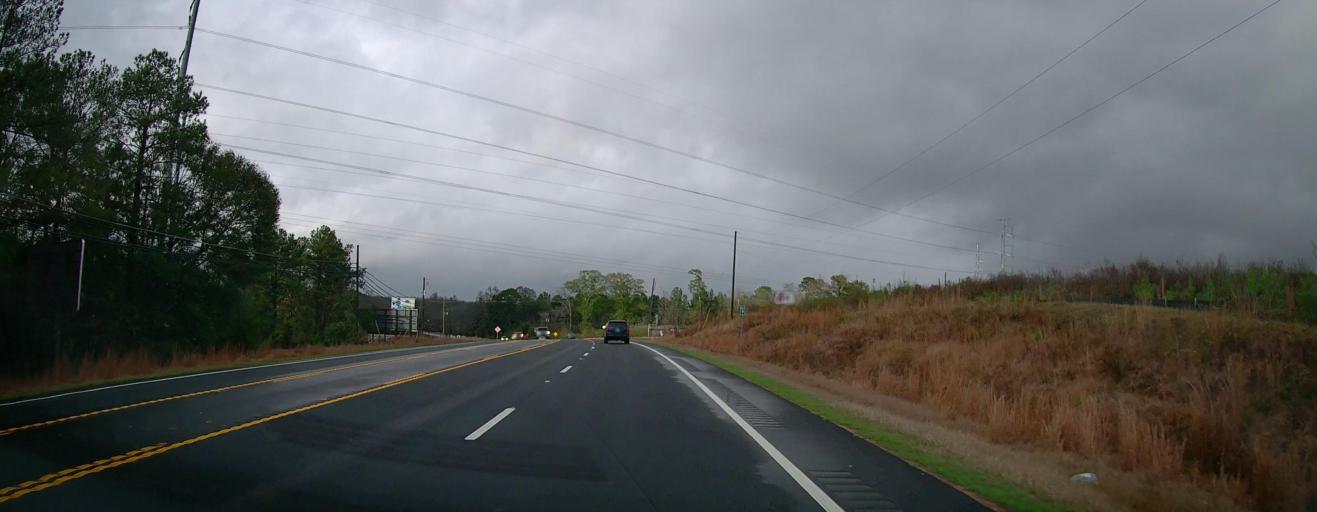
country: US
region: Georgia
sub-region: Clarke County
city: Athens
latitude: 33.9816
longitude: -83.3772
